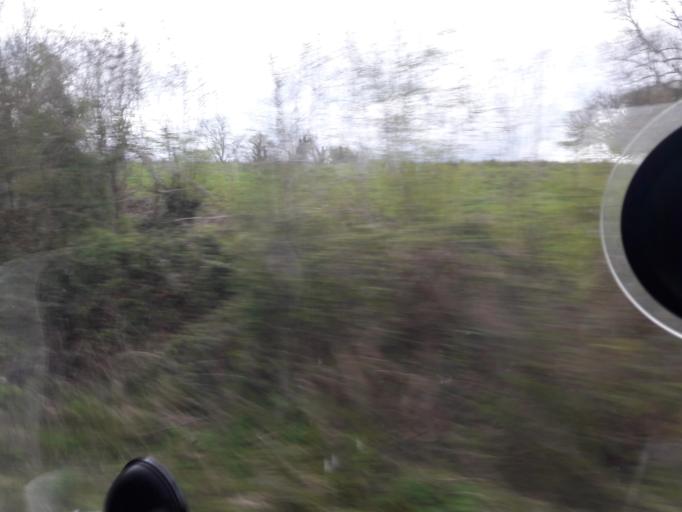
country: IE
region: Leinster
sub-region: An Longfort
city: Longford
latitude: 53.7429
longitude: -7.8227
